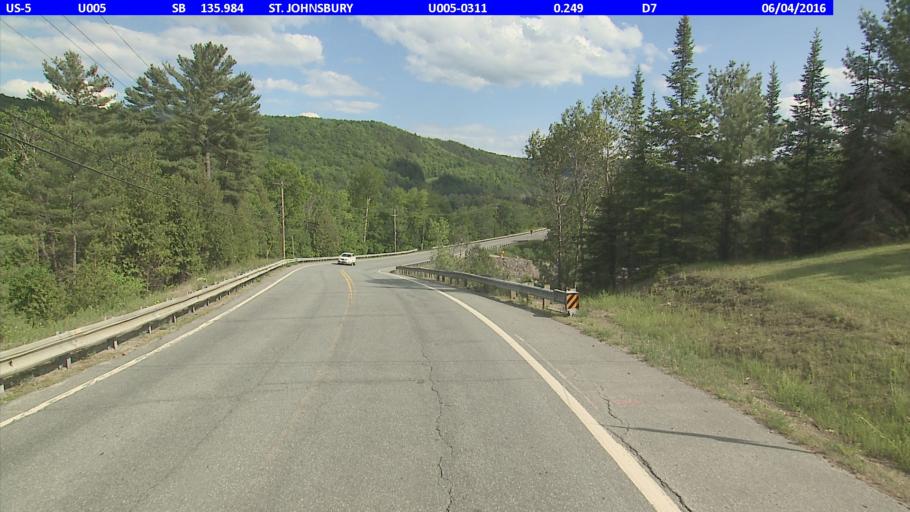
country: US
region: Vermont
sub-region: Caledonia County
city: Saint Johnsbury
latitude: 44.3979
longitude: -72.0249
